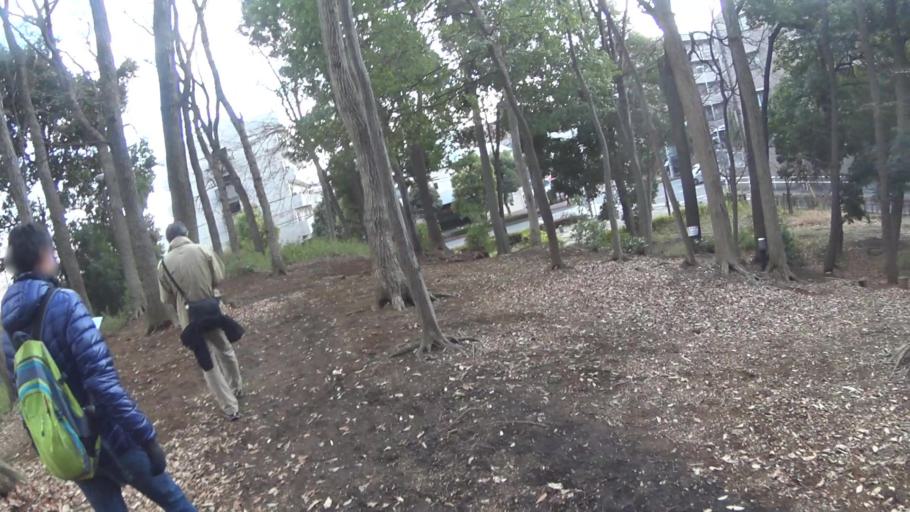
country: JP
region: Saitama
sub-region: Kawaguchi-shi
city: Hatogaya-honcho
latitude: 35.8603
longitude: 139.7011
